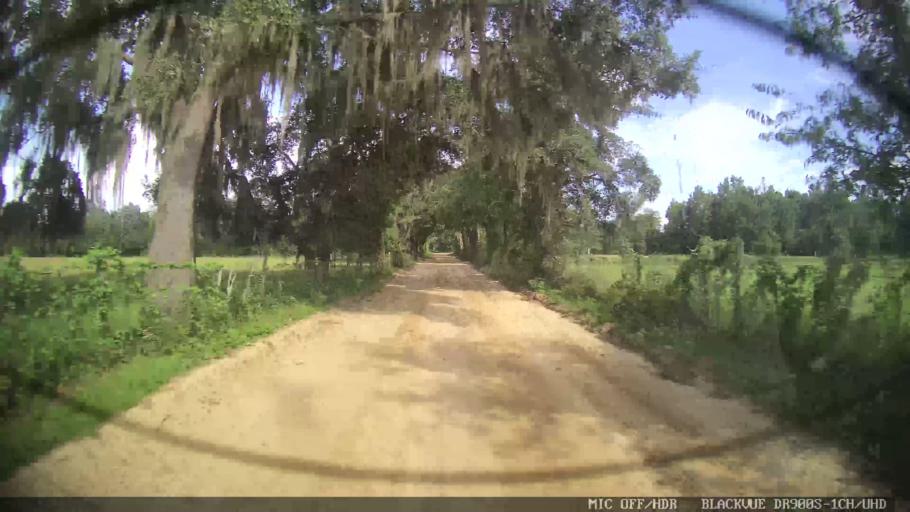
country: US
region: Georgia
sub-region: Echols County
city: Statenville
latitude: 30.6286
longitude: -83.1891
